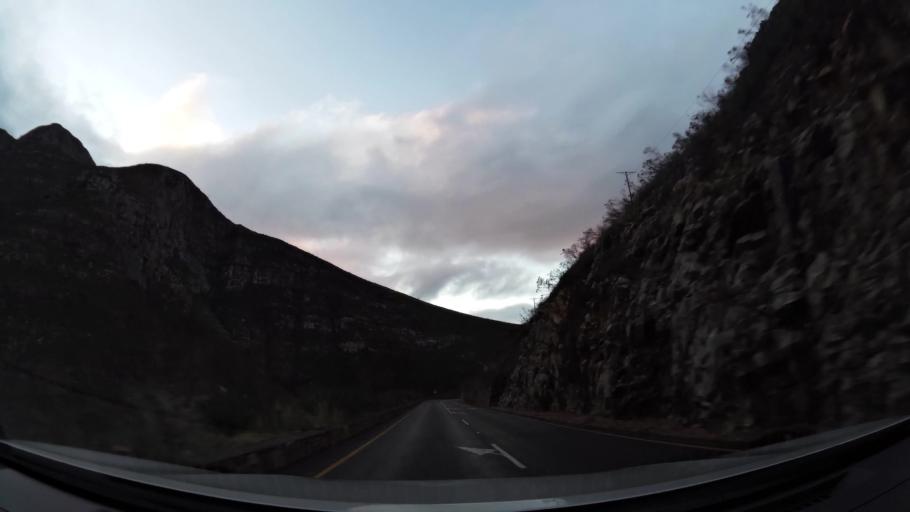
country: ZA
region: Western Cape
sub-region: Overberg District Municipality
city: Swellendam
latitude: -33.9631
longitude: 20.7036
